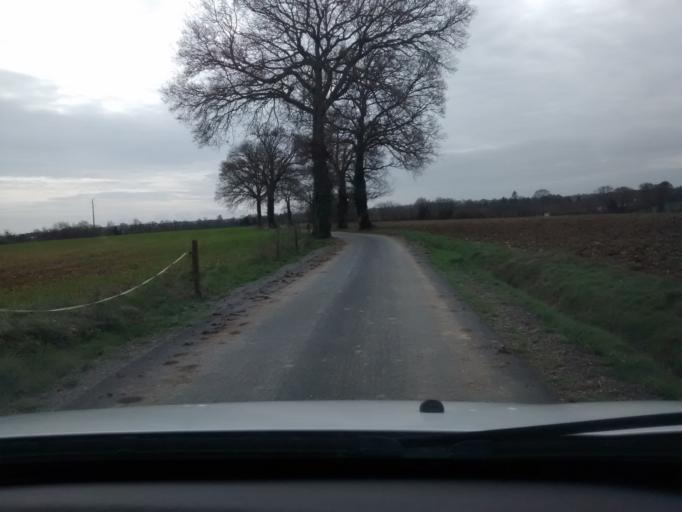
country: FR
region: Brittany
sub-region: Departement d'Ille-et-Vilaine
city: Liffre
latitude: 48.2113
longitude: -1.4775
